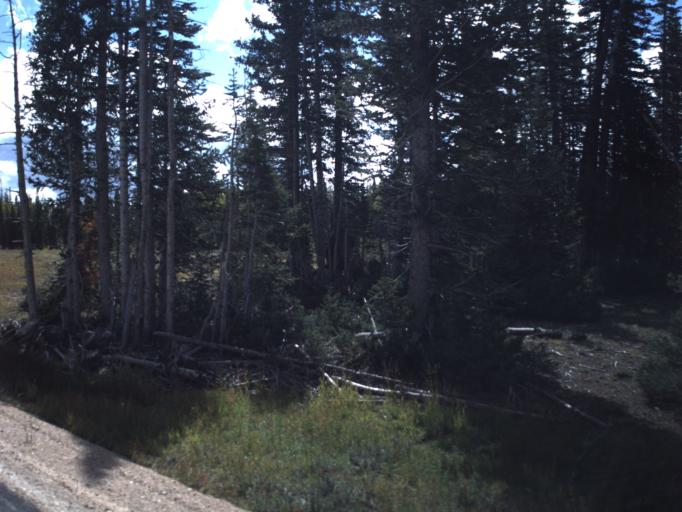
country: US
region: Utah
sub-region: Iron County
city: Parowan
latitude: 37.5595
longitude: -112.7896
